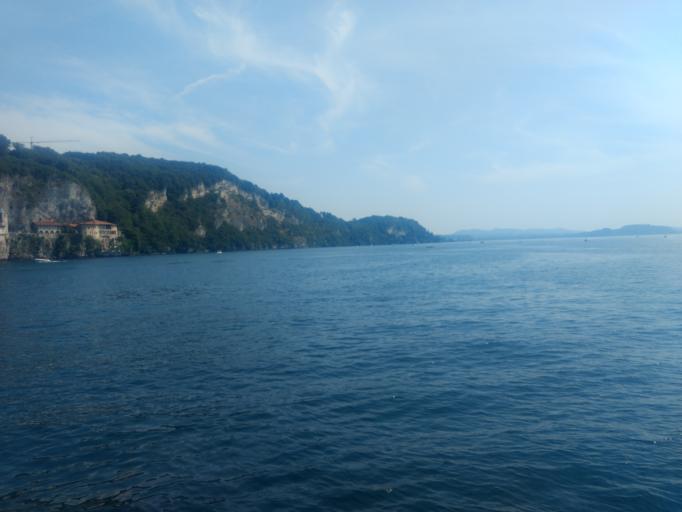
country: IT
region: Lombardy
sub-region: Provincia di Varese
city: Leggiuno
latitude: 45.8783
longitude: 8.5921
